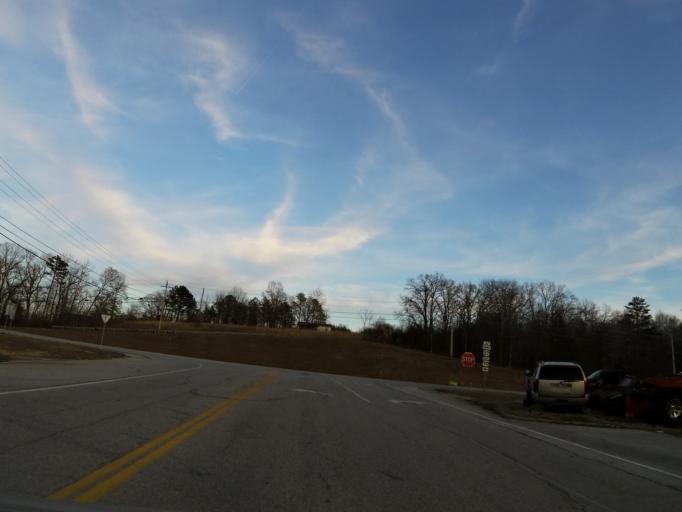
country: US
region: Tennessee
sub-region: Roane County
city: Rockwood
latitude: 35.8445
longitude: -84.7041
